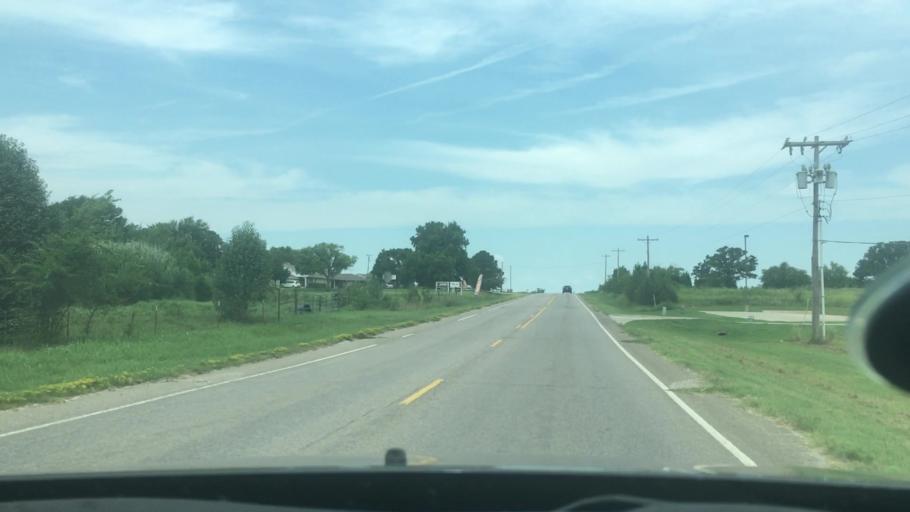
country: US
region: Oklahoma
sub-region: Seminole County
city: Seminole
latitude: 35.2399
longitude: -96.6951
